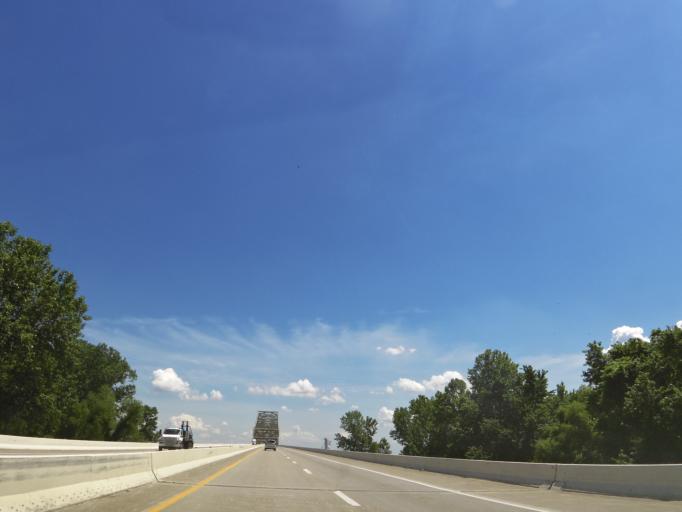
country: US
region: Missouri
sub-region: Pemiscot County
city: Caruthersville
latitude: 36.1198
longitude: -89.6158
